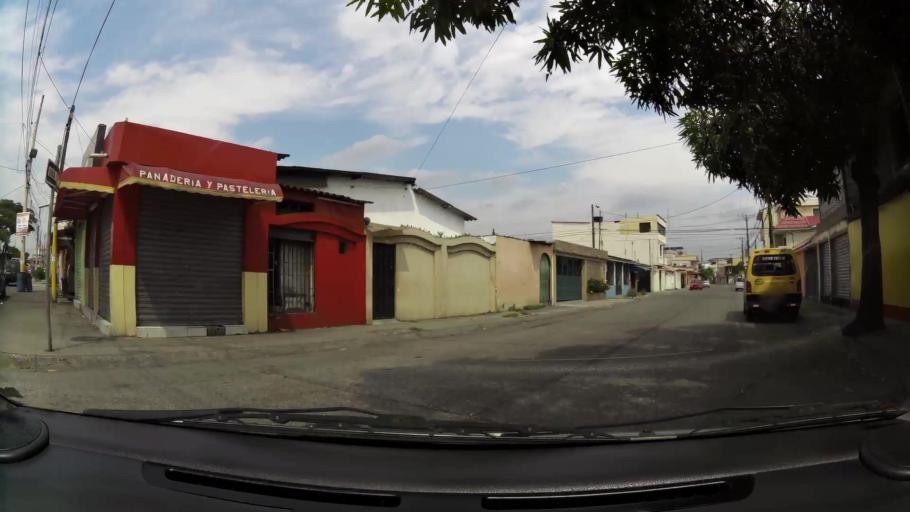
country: EC
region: Guayas
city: Eloy Alfaro
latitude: -2.1215
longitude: -79.8982
